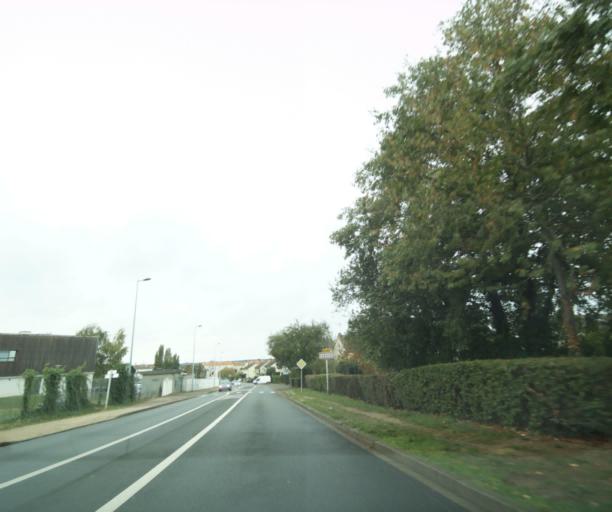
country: FR
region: Centre
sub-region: Departement d'Eure-et-Loir
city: Luray
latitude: 48.7286
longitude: 1.3874
